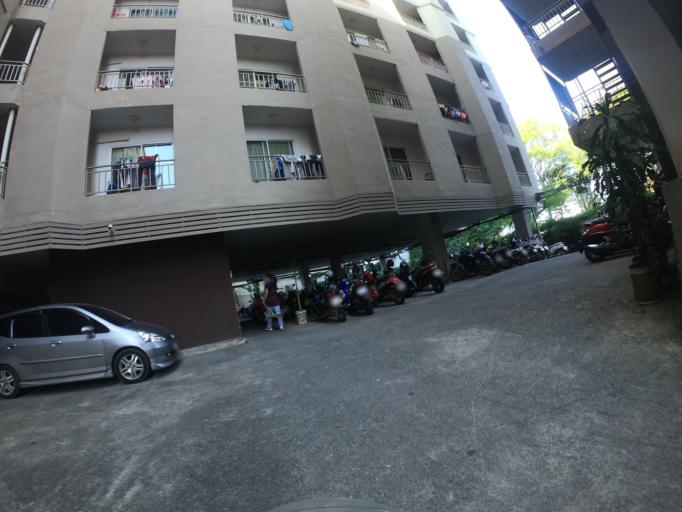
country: TH
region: Chiang Mai
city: Chiang Mai
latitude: 18.8026
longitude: 98.9845
